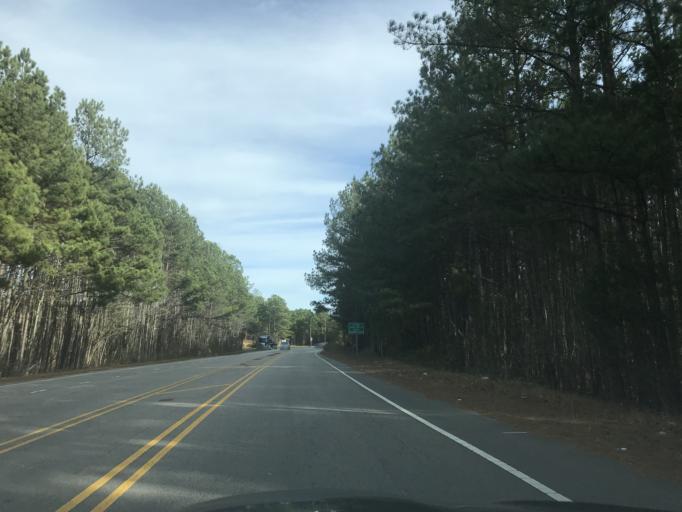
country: US
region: North Carolina
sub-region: Wake County
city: Cary
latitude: 35.7807
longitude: -78.7456
